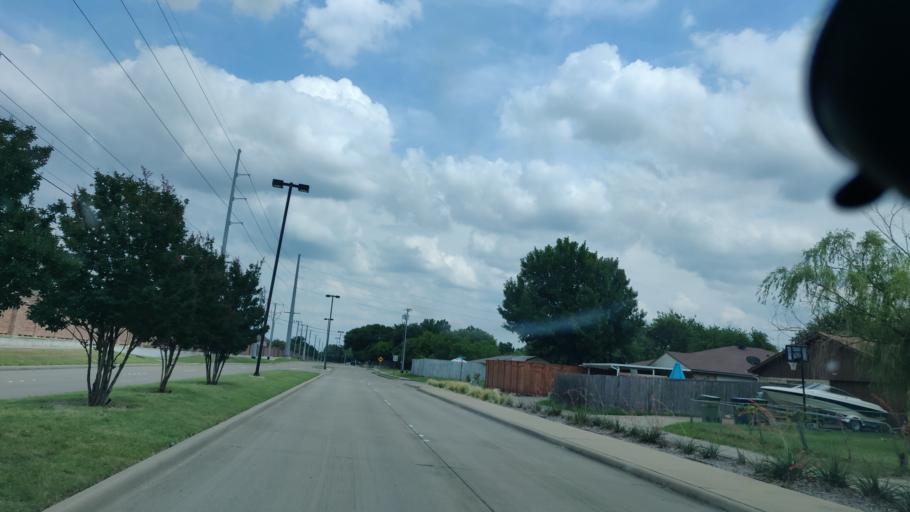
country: US
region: Texas
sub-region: Dallas County
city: Garland
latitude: 32.9394
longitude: -96.6111
